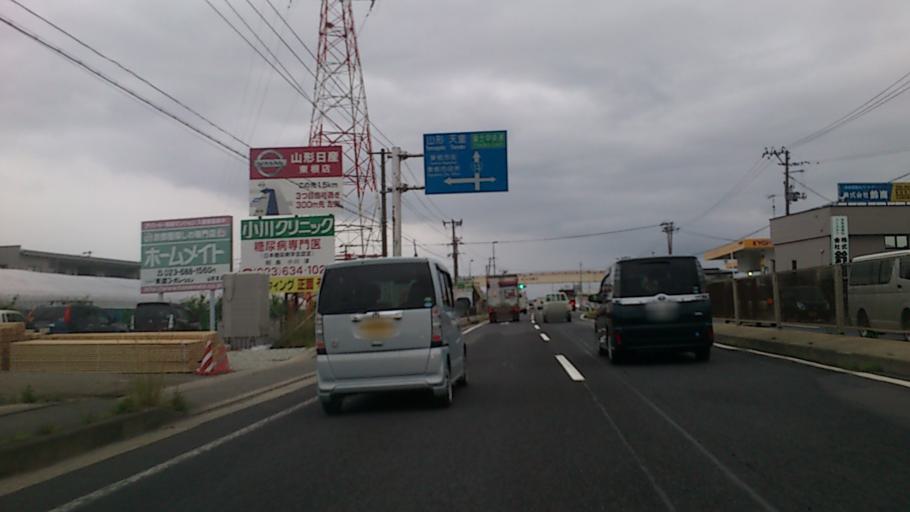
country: JP
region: Yamagata
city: Higashine
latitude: 38.4372
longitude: 140.3791
